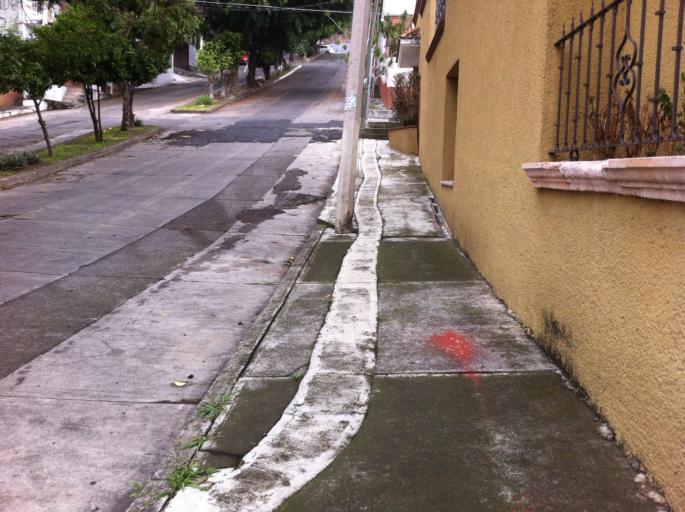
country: MX
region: Michoacan
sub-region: Morelia
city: Montana Monarca (Punta Altozano)
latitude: 19.6804
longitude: -101.1710
